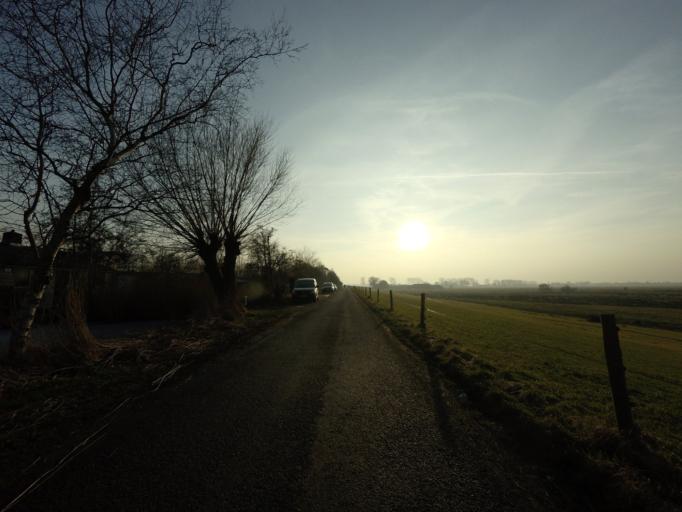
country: NL
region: North Holland
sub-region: Gemeente Ouder-Amstel
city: Ouderkerk aan de Amstel
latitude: 52.2403
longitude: 4.9296
